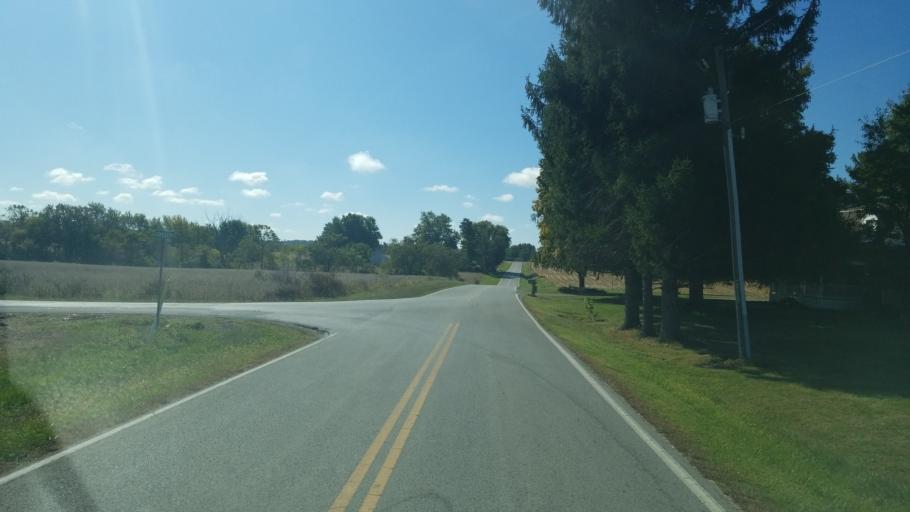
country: US
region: Ohio
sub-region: Highland County
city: Leesburg
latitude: 39.2932
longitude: -83.5798
